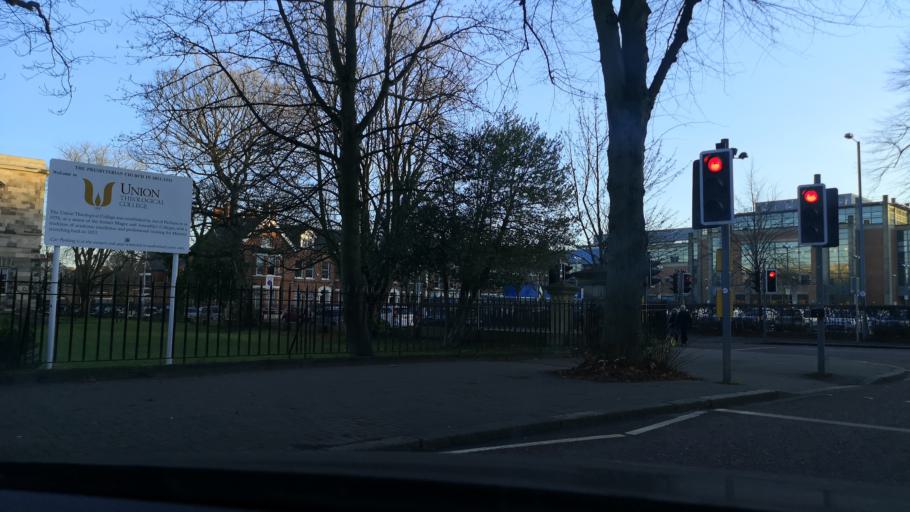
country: GB
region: Northern Ireland
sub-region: City of Belfast
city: Belfast
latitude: 54.5852
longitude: -5.9325
